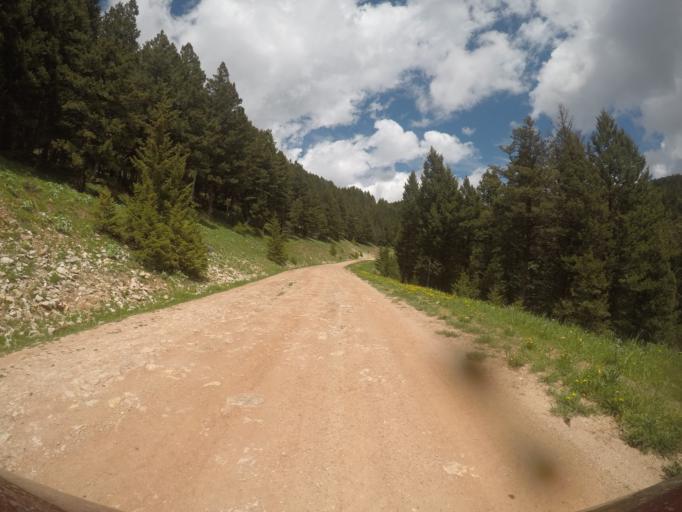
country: US
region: Wyoming
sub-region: Big Horn County
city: Lovell
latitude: 45.1691
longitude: -108.4154
